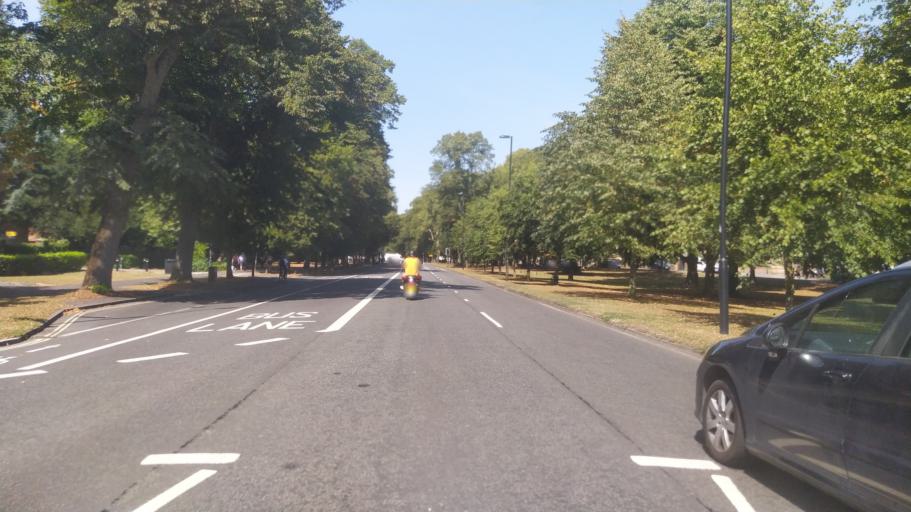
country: GB
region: England
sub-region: Southampton
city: Southampton
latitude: 50.9148
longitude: -1.4024
